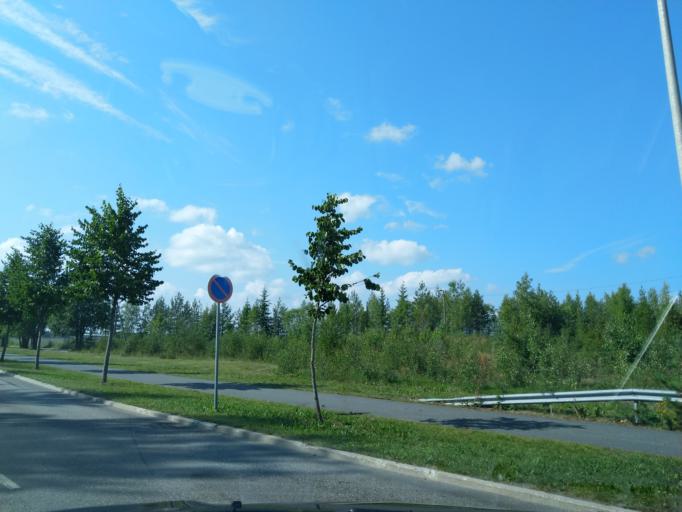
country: FI
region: South Karelia
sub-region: Lappeenranta
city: Lappeenranta
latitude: 61.0374
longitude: 28.1228
